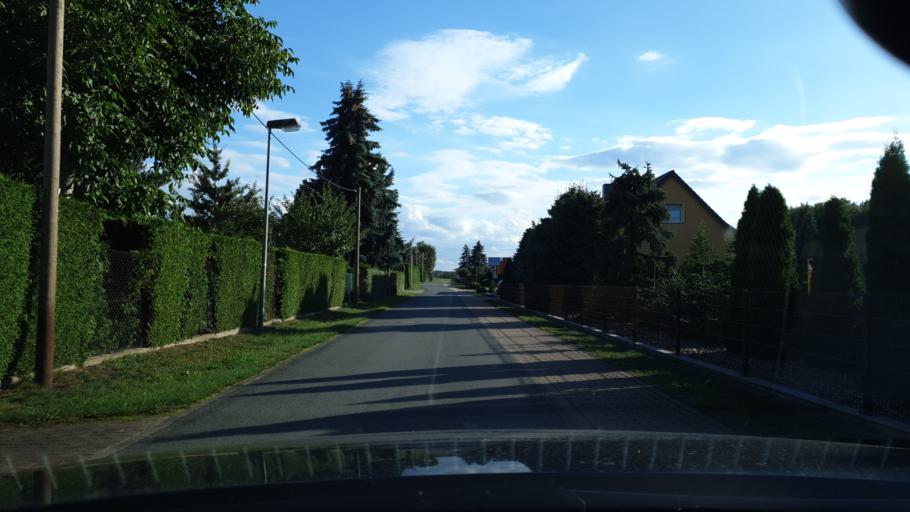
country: DE
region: Saxony-Anhalt
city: Radis
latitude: 51.7544
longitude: 12.5056
